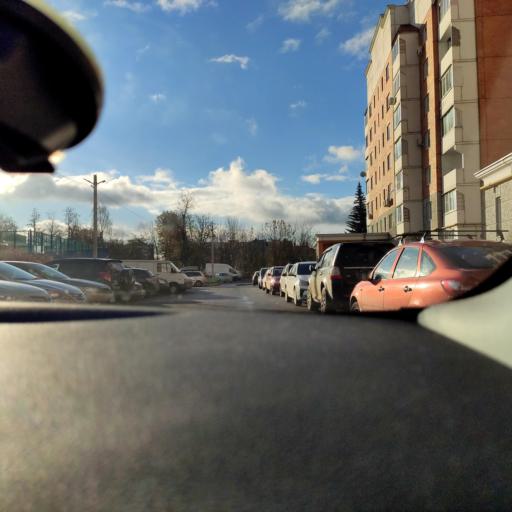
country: RU
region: Moskovskaya
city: Shcherbinka
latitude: 55.4737
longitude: 37.6085
